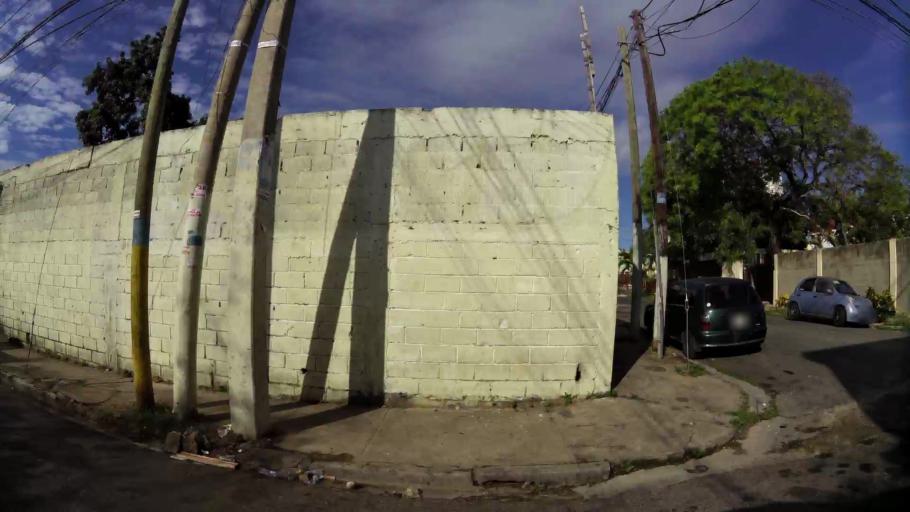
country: DO
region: Santo Domingo
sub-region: Santo Domingo
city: Santo Domingo Este
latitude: 18.4867
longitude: -69.8570
